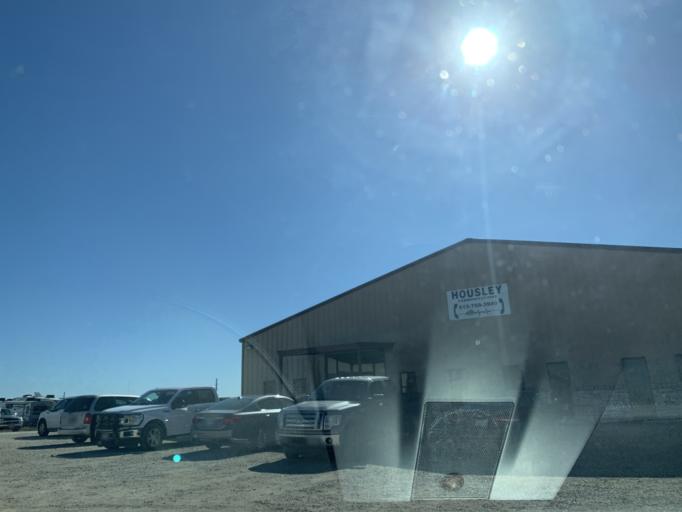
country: US
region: Texas
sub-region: Williamson County
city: Hutto
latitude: 30.5479
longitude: -97.5693
